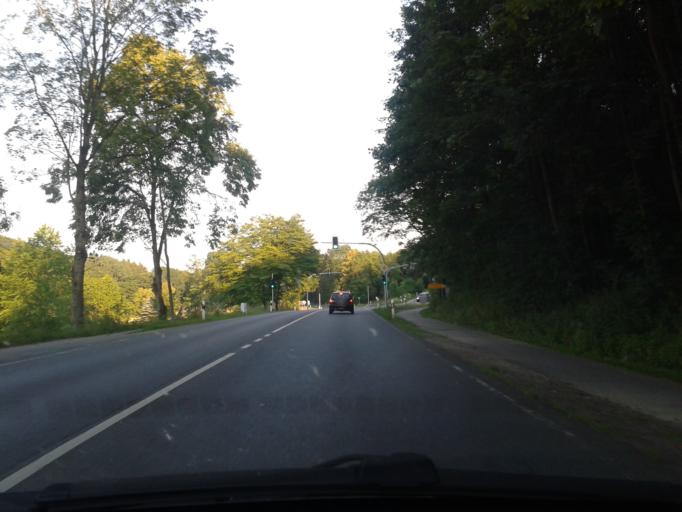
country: DE
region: North Rhine-Westphalia
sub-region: Regierungsbezirk Detmold
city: Horn
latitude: 51.8979
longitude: 8.9350
